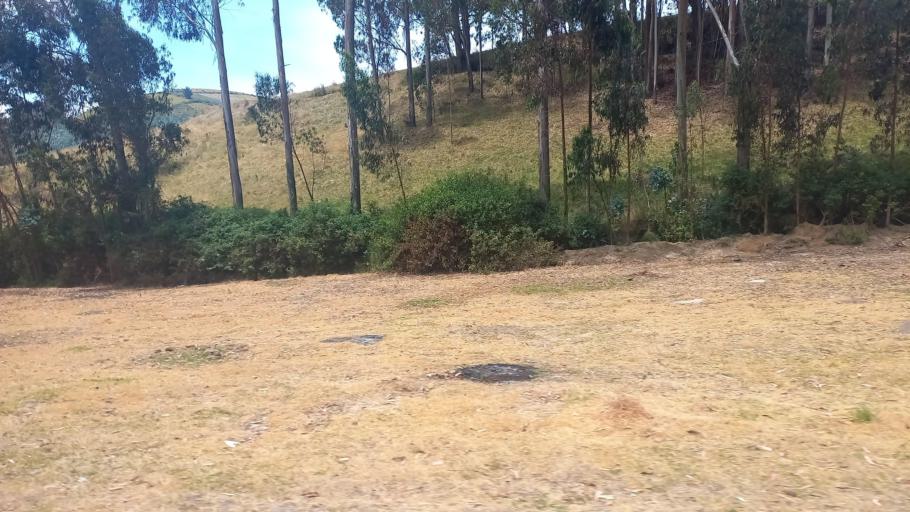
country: EC
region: Pichincha
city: Cayambe
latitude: 0.1773
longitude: -78.0913
